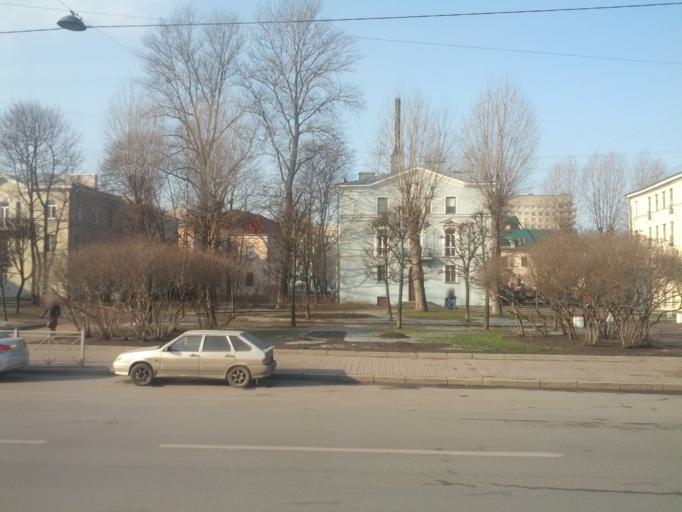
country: RU
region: Leningrad
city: Kalininskiy
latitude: 59.9526
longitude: 30.4148
